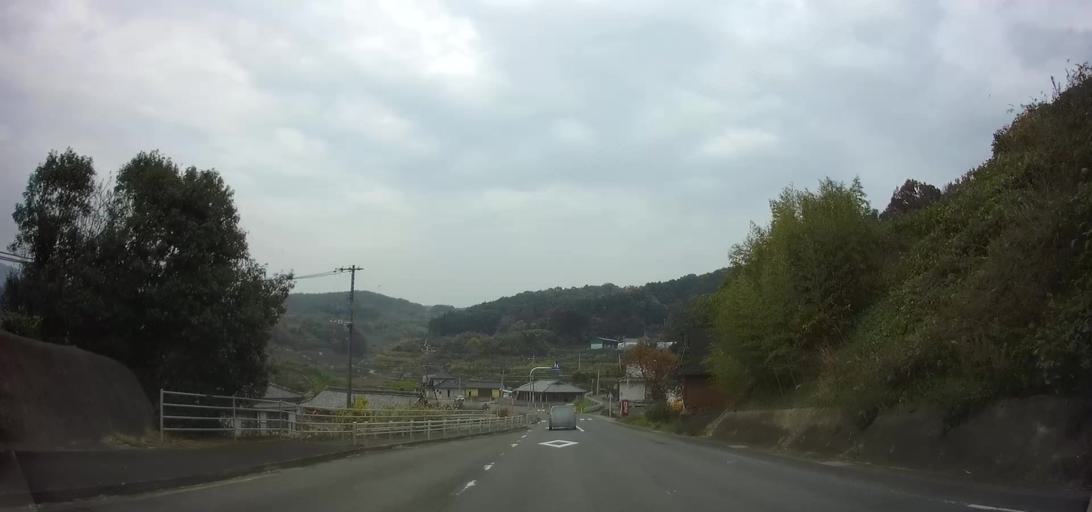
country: JP
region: Nagasaki
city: Shimabara
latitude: 32.7053
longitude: 130.1873
